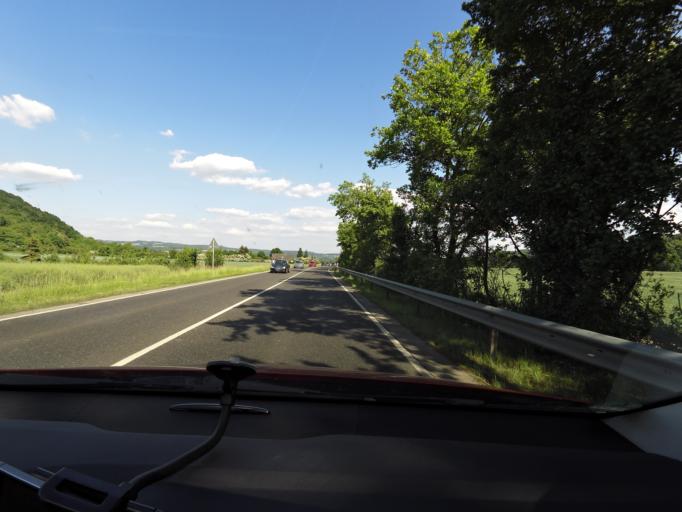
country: DE
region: Rheinland-Pfalz
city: Sinzig
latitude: 50.5539
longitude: 7.2273
